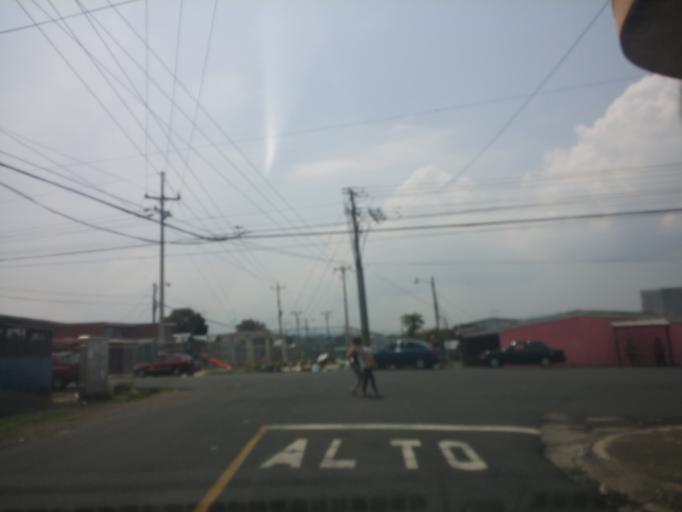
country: CR
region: Heredia
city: San Francisco
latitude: 9.9819
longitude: -84.1188
